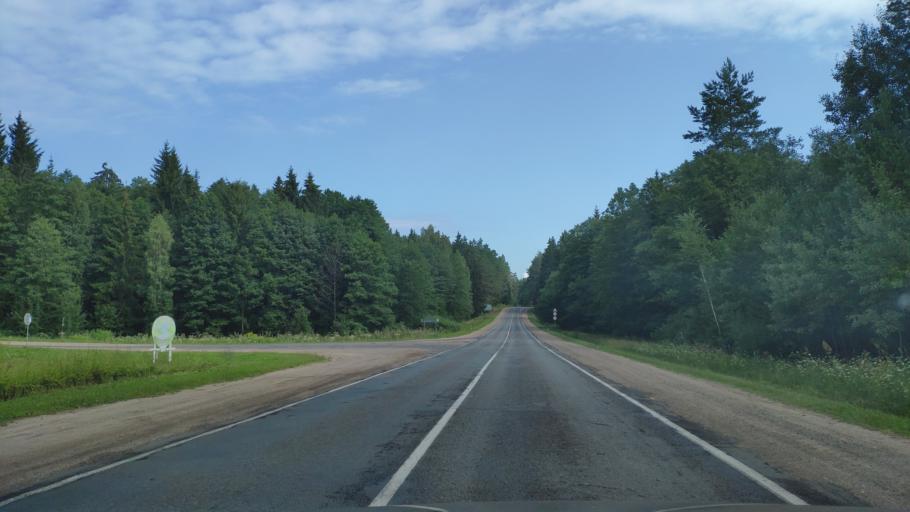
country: BY
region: Minsk
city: Zaslawye
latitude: 53.9738
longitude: 27.2486
